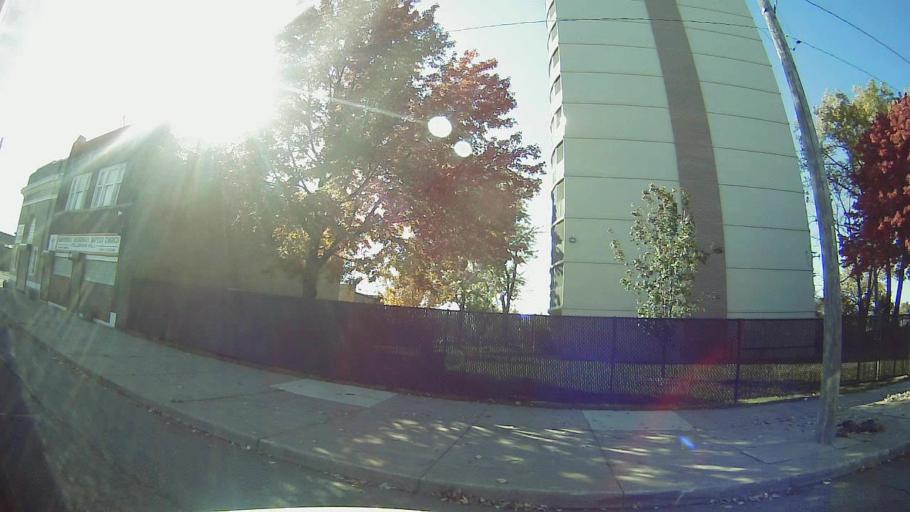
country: US
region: Michigan
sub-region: Wayne County
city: Highland Park
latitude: 42.3615
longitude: -83.0940
